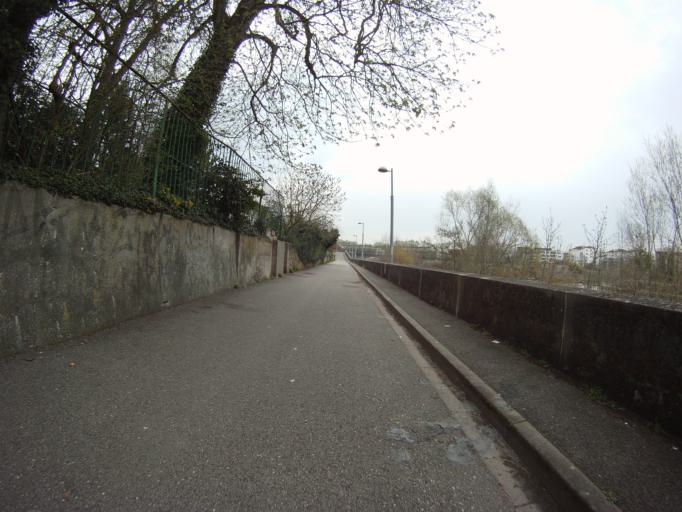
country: FR
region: Lorraine
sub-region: Departement de Meurthe-et-Moselle
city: Saint-Max
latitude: 48.7015
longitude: 6.1968
